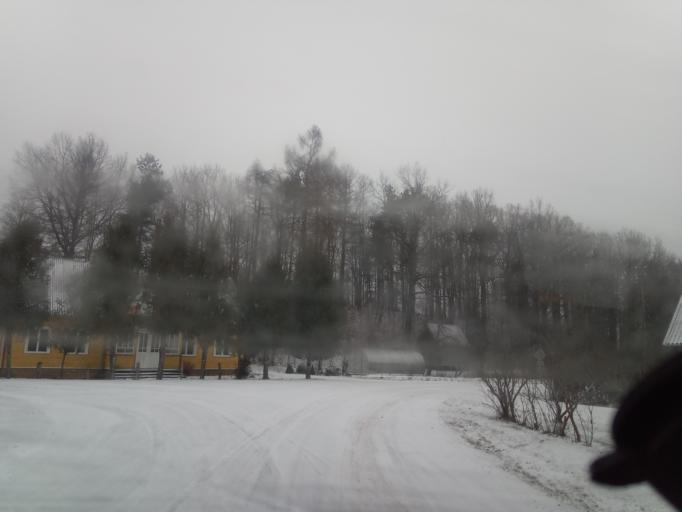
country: LT
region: Utenos apskritis
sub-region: Anyksciai
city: Anyksciai
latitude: 55.4217
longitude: 25.1093
